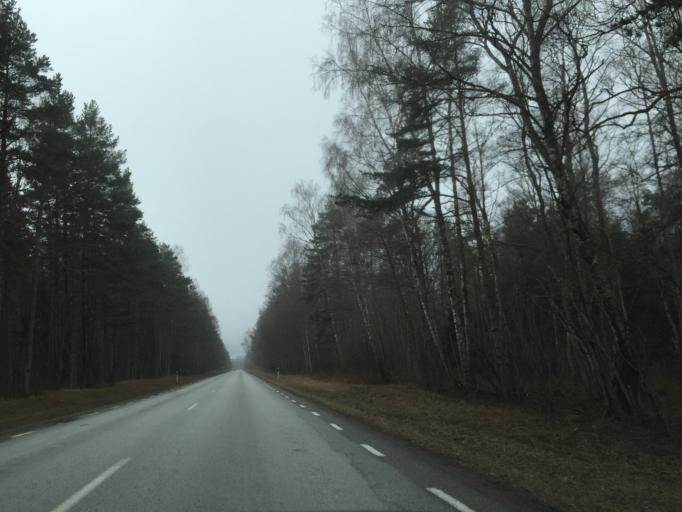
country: EE
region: Saare
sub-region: Kuressaare linn
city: Kuressaare
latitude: 58.1904
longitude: 22.2668
